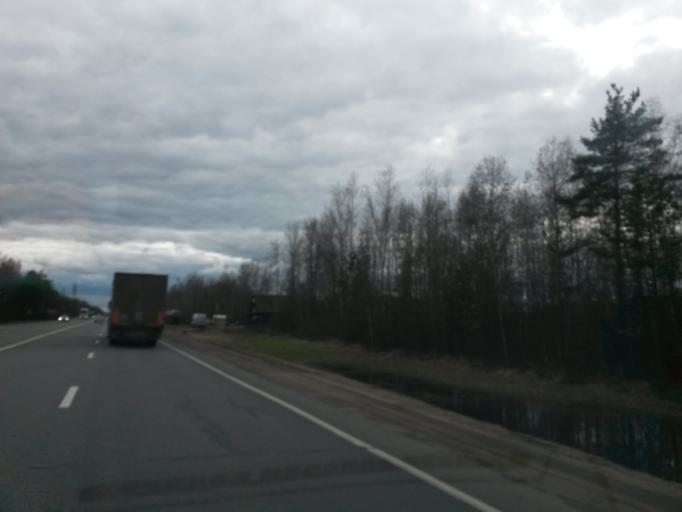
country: RU
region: Jaroslavl
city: Rostov
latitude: 57.2417
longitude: 39.4760
